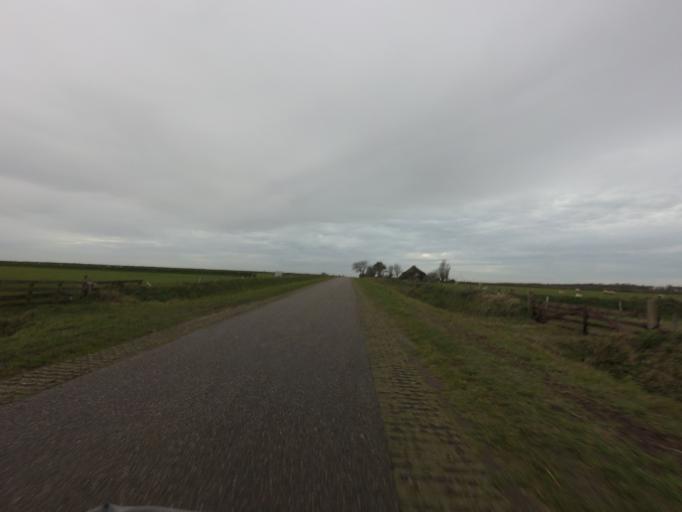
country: NL
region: North Holland
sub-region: Gemeente Texel
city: Den Burg
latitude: 53.0450
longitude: 4.8128
